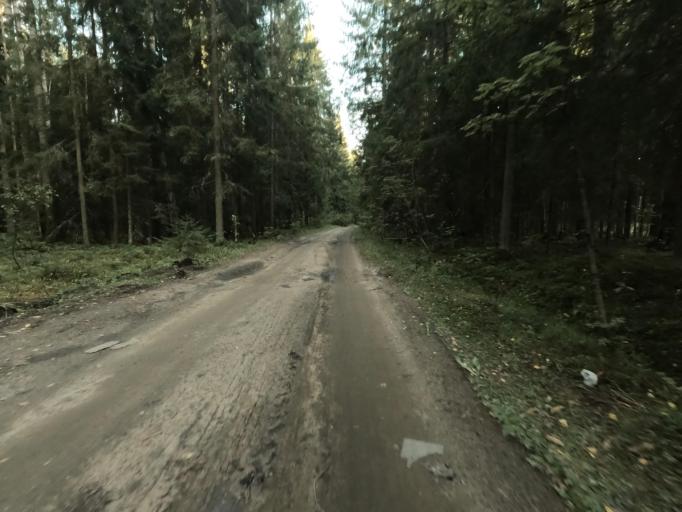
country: RU
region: Leningrad
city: Otradnoye
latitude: 59.8275
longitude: 30.7715
